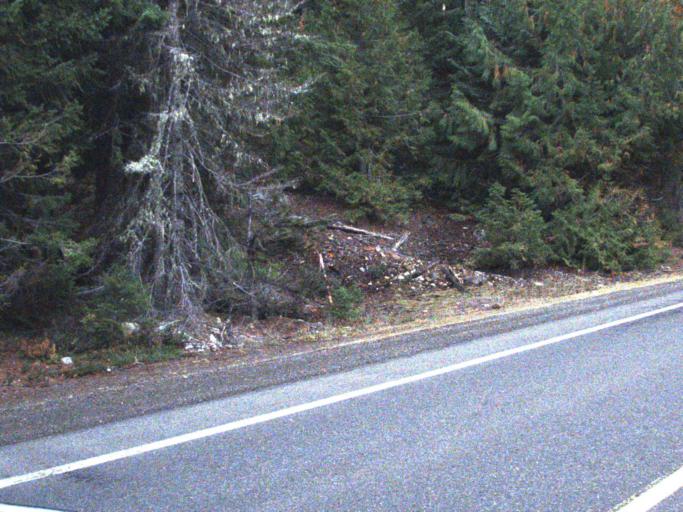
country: US
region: Washington
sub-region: Yakima County
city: Tieton
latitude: 46.6389
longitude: -121.4539
